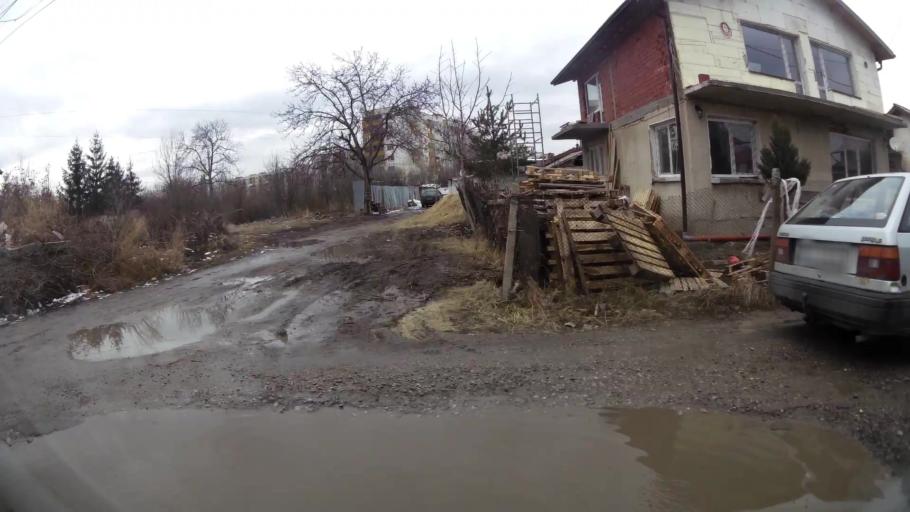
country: BG
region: Sofia-Capital
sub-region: Stolichna Obshtina
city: Sofia
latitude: 42.7228
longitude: 23.2786
